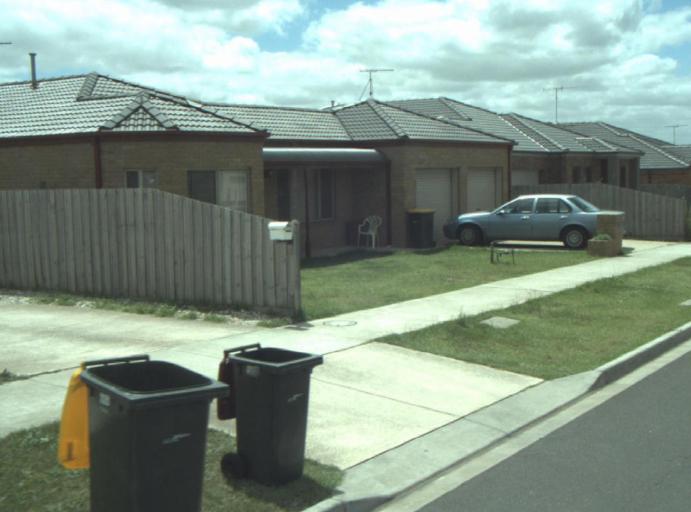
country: AU
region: Victoria
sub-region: Greater Geelong
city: Wandana Heights
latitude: -38.2104
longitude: 144.3114
